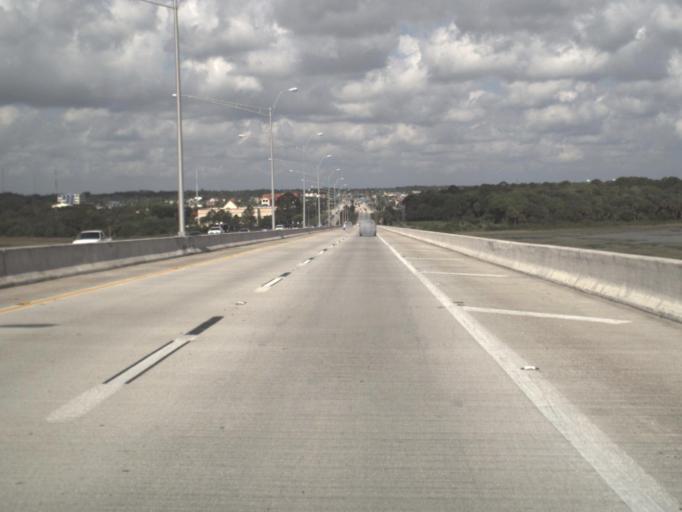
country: US
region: Florida
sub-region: Saint Johns County
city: Saint Augustine South
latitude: 29.8672
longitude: -81.3092
